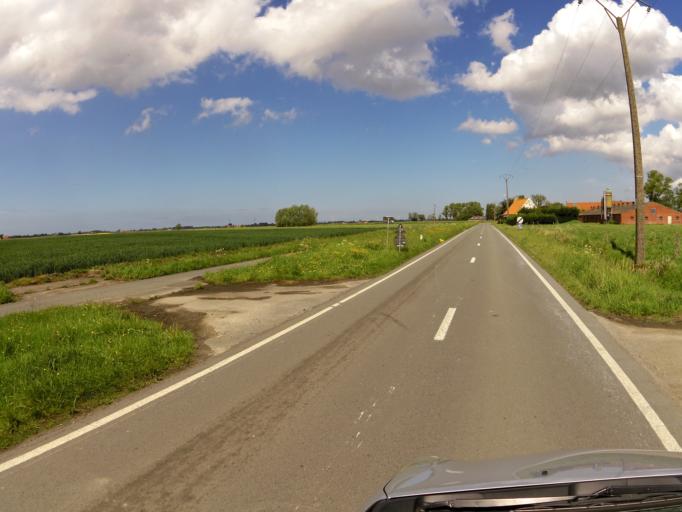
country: BE
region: Flanders
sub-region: Provincie West-Vlaanderen
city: Koekelare
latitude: 51.1155
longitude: 2.9390
